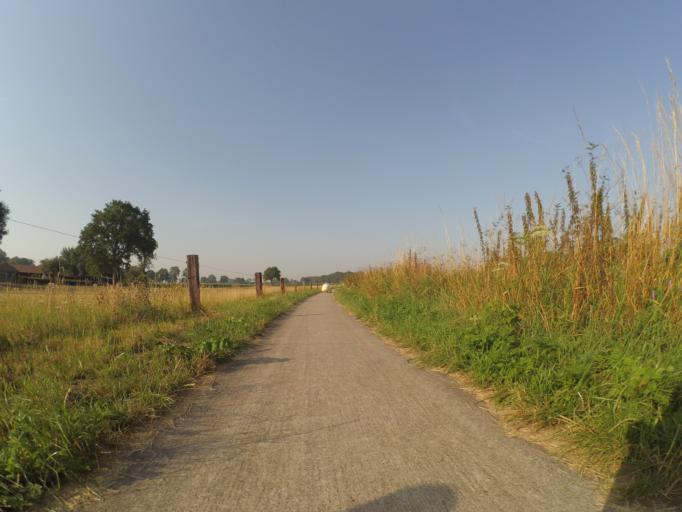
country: NL
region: Overijssel
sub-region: Gemeente Wierden
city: Wierden
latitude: 52.3237
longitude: 6.5872
